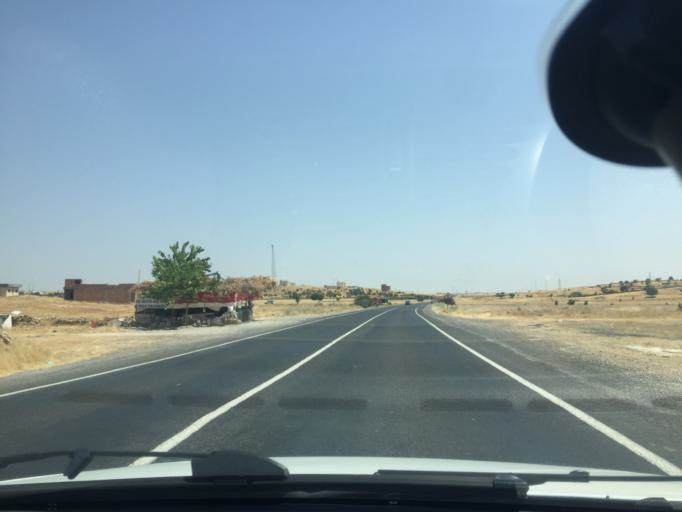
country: TR
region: Mardin
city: Acirli
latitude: 37.4465
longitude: 41.2803
